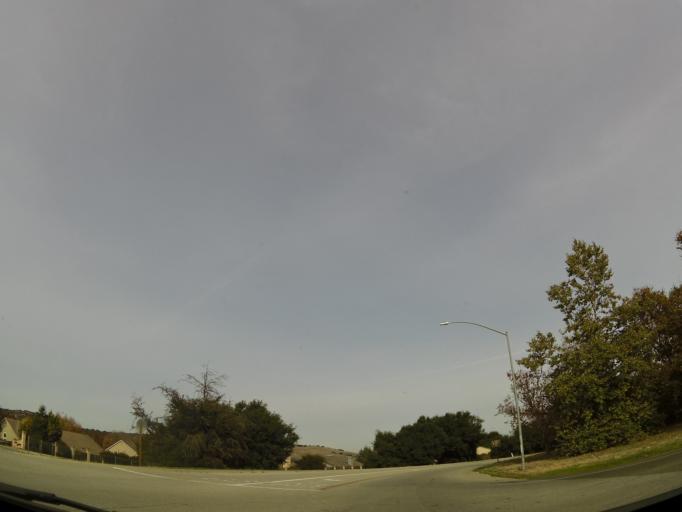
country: US
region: California
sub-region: Monterey County
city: Salinas
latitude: 36.6066
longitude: -121.6947
